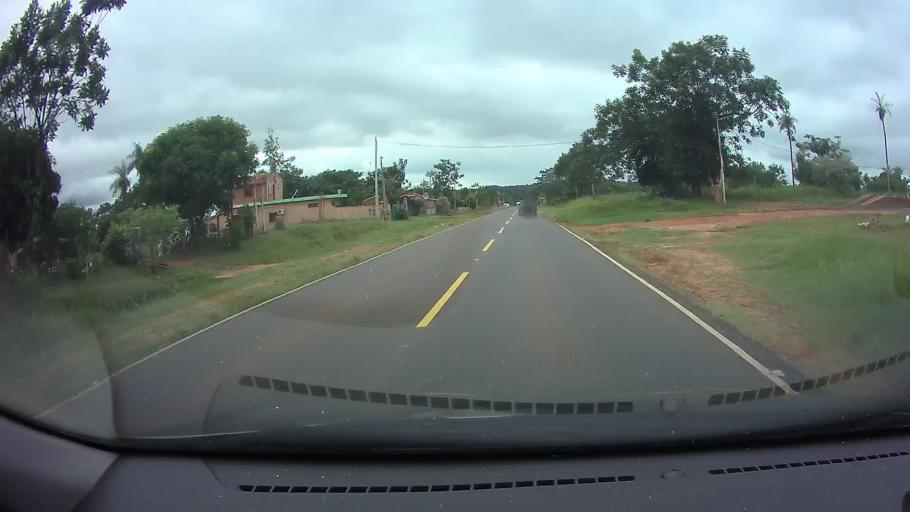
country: PY
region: Paraguari
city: Carapegua
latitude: -25.7325
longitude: -57.3042
